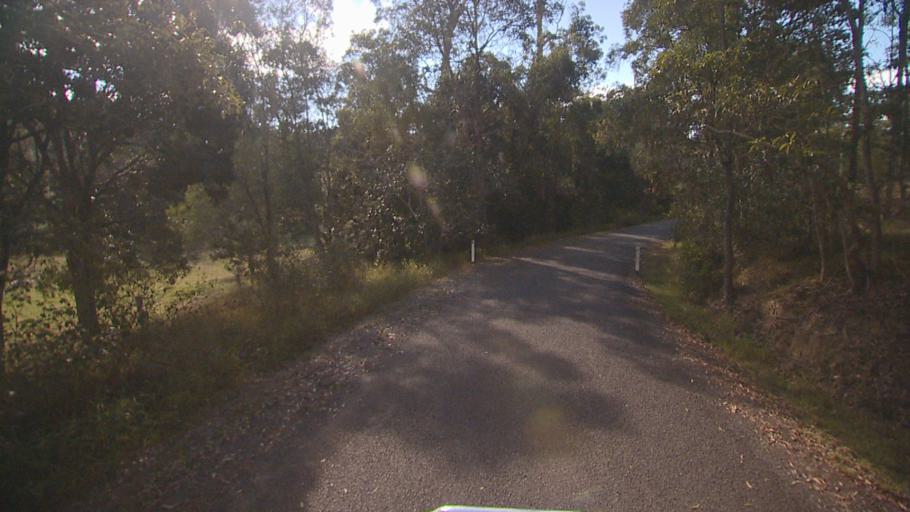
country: AU
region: Queensland
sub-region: Logan
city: Windaroo
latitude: -27.7775
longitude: 153.1742
